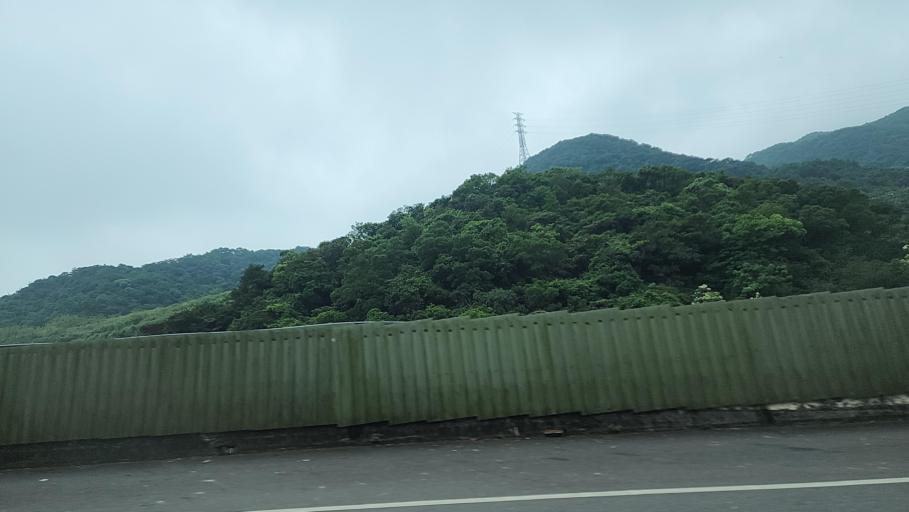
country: TW
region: Taiwan
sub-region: Keelung
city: Keelung
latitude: 25.1644
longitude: 121.6843
